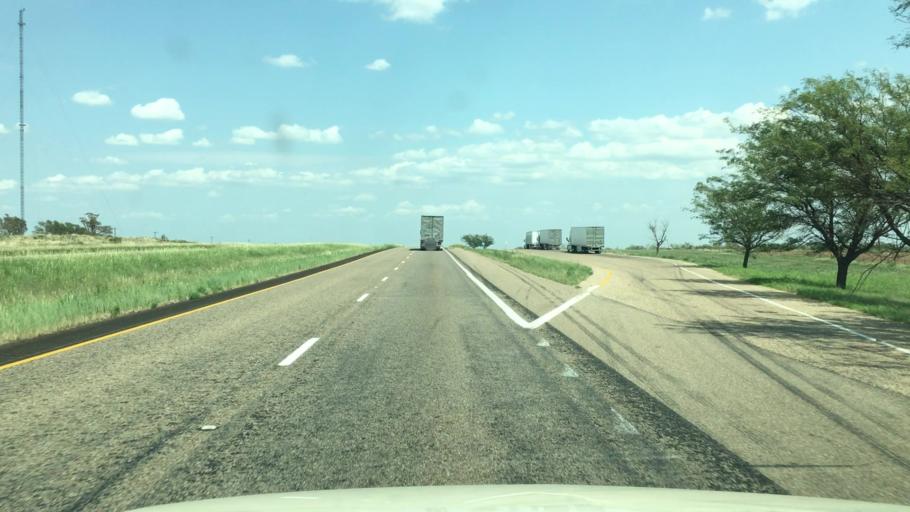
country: US
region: Texas
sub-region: Armstrong County
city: Claude
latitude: 35.0328
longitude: -101.1529
